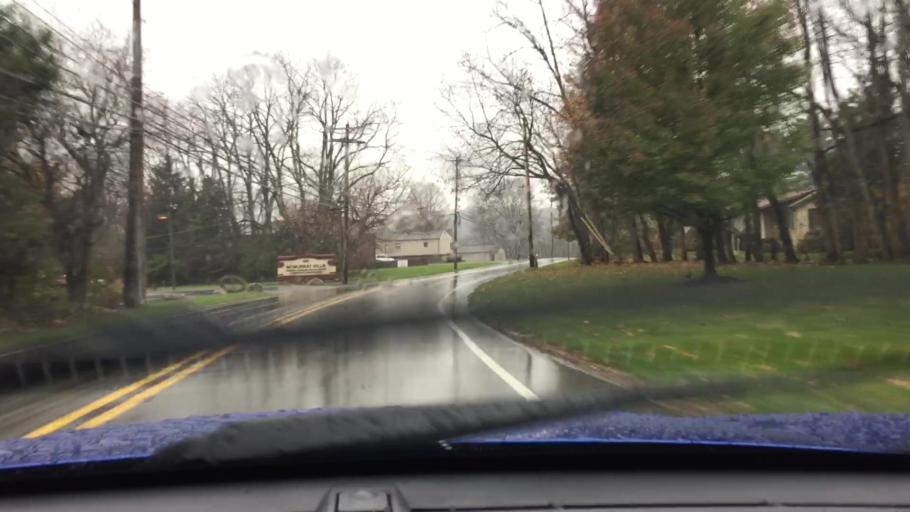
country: US
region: Pennsylvania
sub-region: Washington County
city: Thompsonville
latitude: 40.2751
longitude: -80.1331
